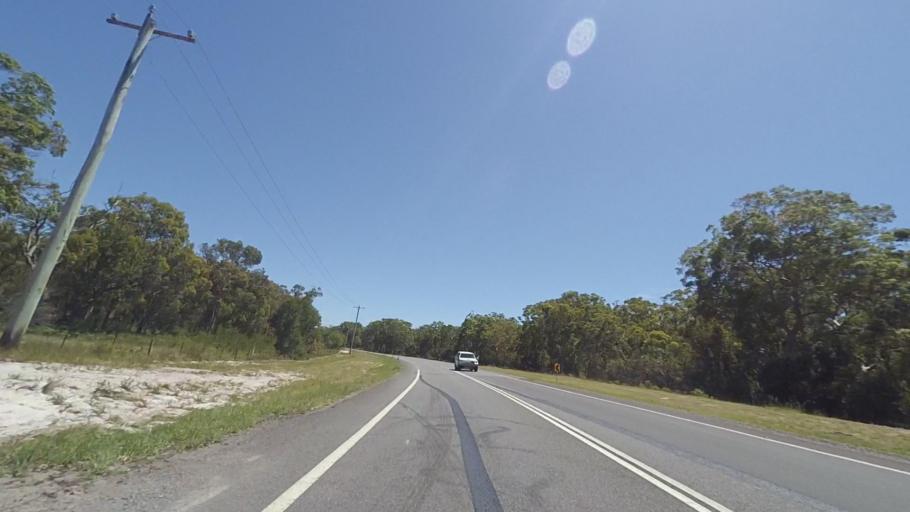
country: AU
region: New South Wales
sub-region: Port Stephens Shire
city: Medowie
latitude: -32.7805
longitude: 151.8590
